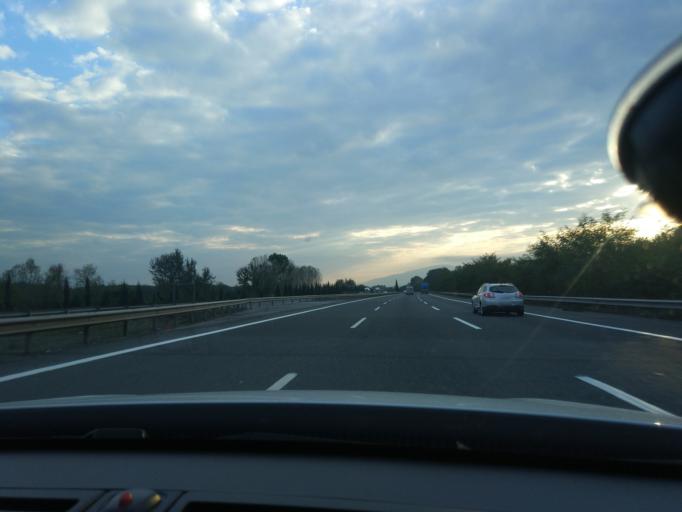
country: TR
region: Sakarya
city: Akyazi
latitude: 40.7421
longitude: 30.6594
